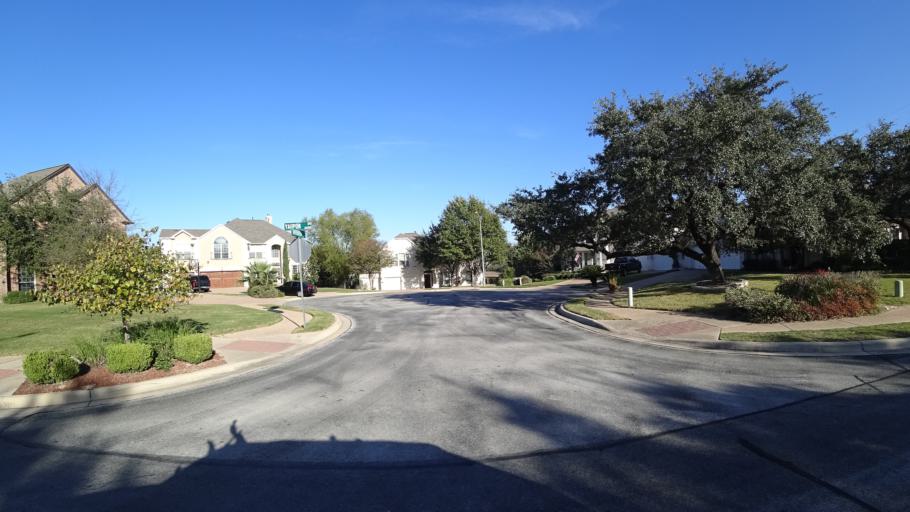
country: US
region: Texas
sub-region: Williamson County
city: Jollyville
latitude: 30.4020
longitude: -97.7763
